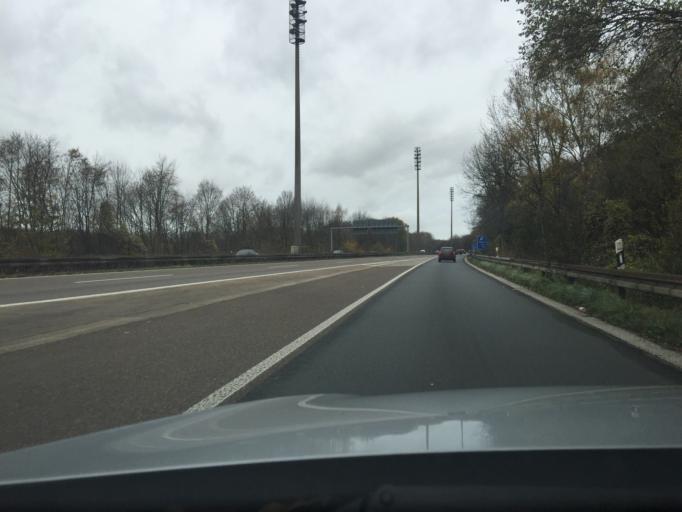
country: DE
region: North Rhine-Westphalia
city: Wulfrath
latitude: 51.2468
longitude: 7.0921
